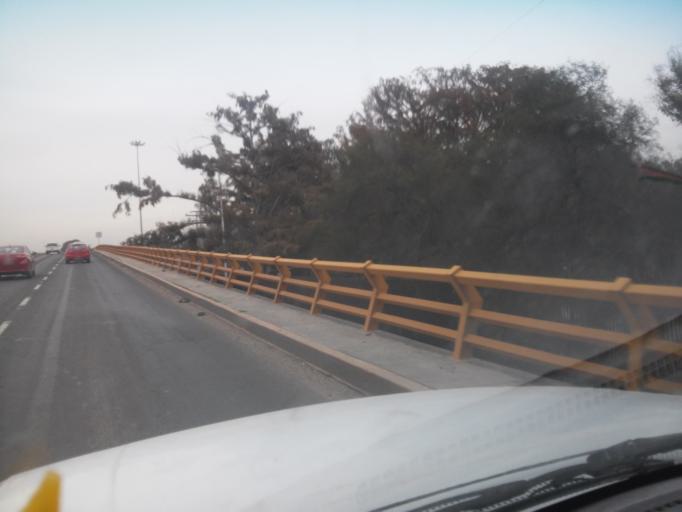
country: MX
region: Durango
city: Victoria de Durango
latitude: 24.0288
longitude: -104.6880
